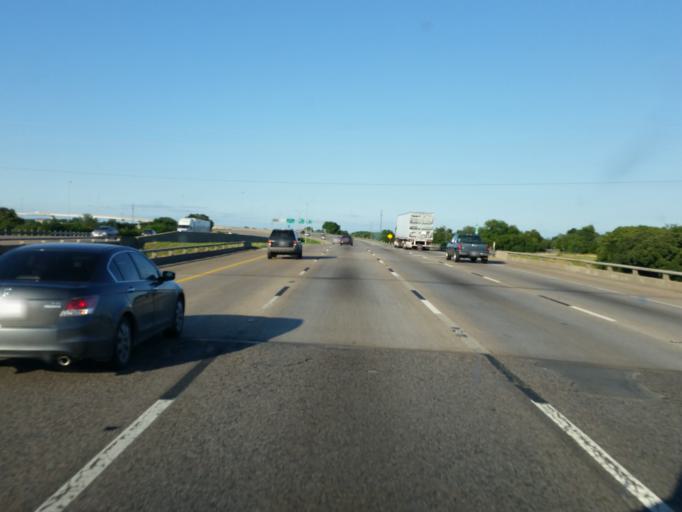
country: US
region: Texas
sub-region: Dallas County
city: Balch Springs
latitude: 32.6863
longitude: -96.6405
